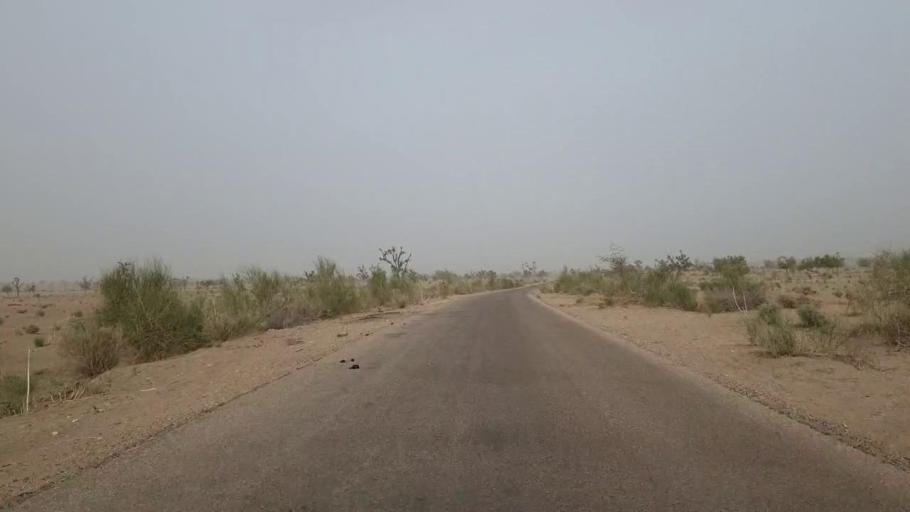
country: PK
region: Sindh
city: Islamkot
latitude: 24.5489
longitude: 70.3616
